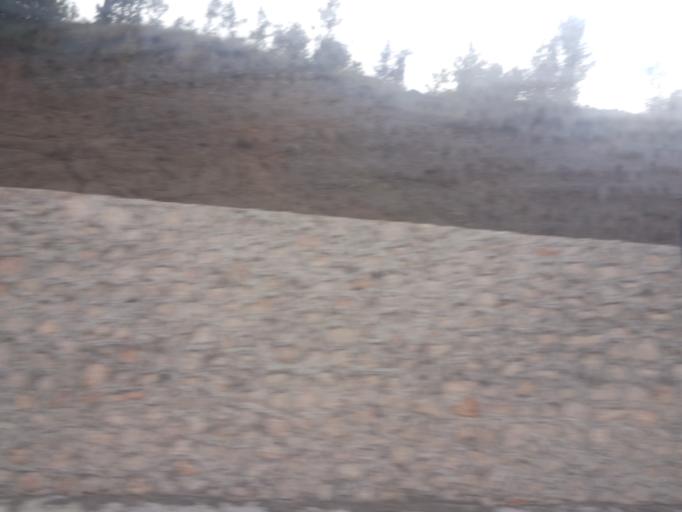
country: TR
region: Tokat
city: Bereketli
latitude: 40.5352
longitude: 37.3065
